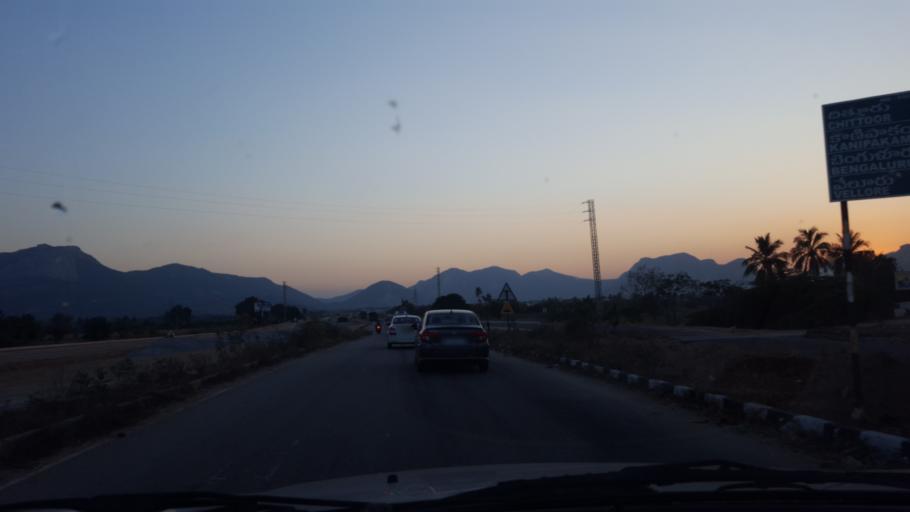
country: IN
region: Andhra Pradesh
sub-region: Chittoor
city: Narasingapuram
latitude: 13.5971
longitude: 79.3497
